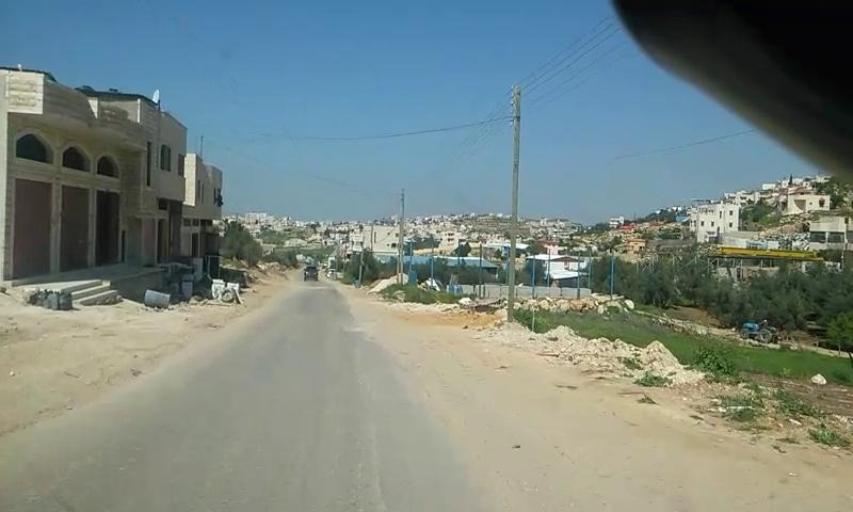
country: PS
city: Dayr Samit
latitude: 31.5084
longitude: 34.9702
